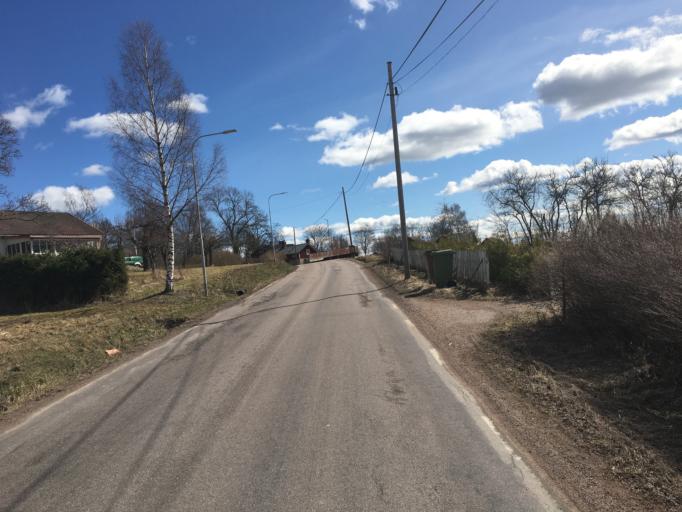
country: SE
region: Gaevleborg
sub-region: Hofors Kommun
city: Hofors
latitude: 60.5152
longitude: 16.4425
